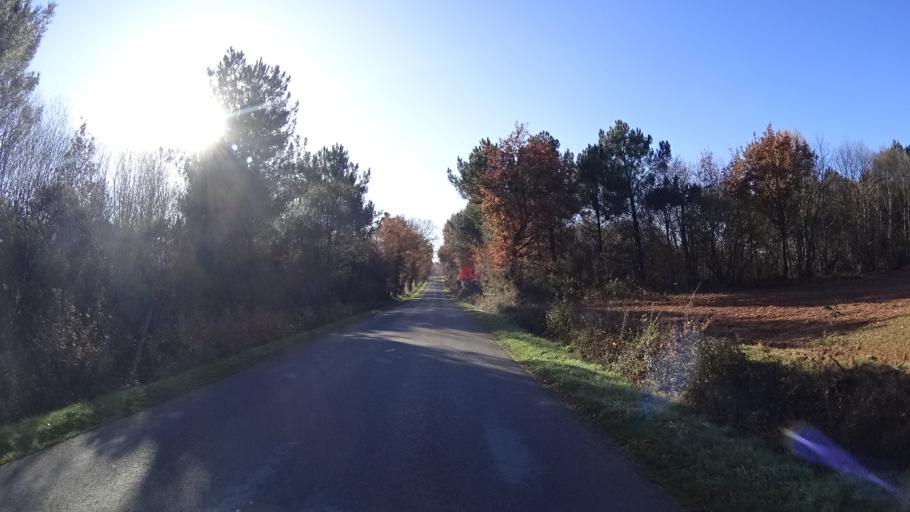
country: FR
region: Brittany
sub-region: Departement du Morbihan
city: Saint-Martin-sur-Oust
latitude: 47.7888
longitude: -2.2095
